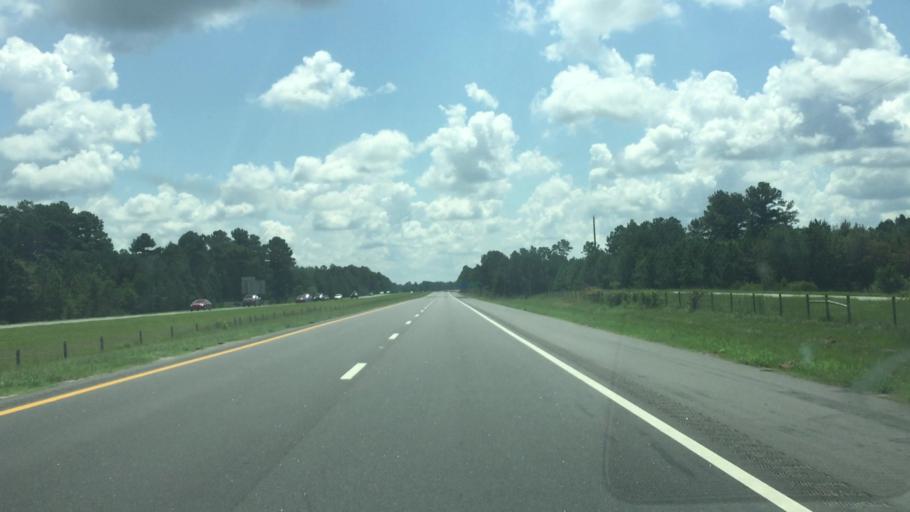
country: US
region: North Carolina
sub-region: Robeson County
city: Maxton
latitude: 34.6995
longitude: -79.2930
